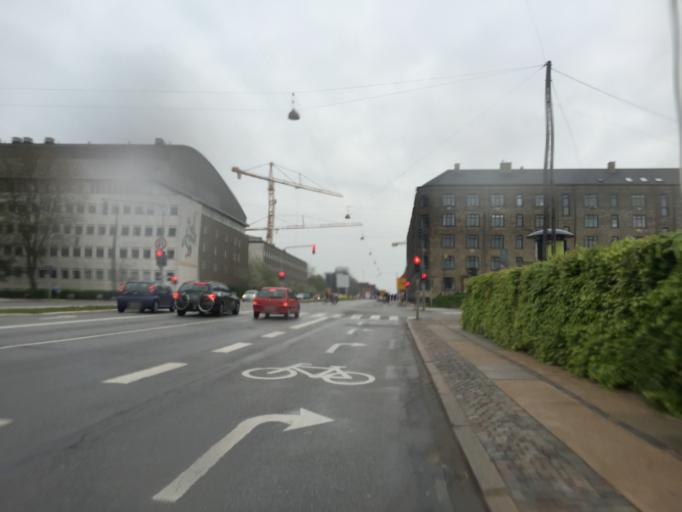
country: DK
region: Capital Region
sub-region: Kobenhavn
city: Copenhagen
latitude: 55.7036
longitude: 12.5591
